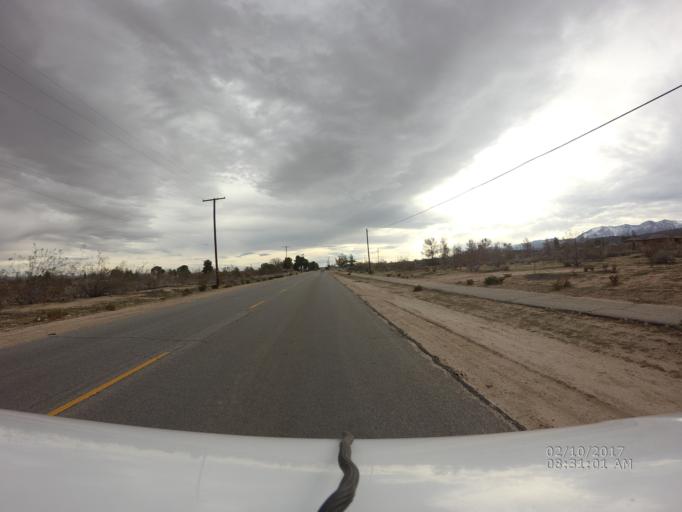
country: US
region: California
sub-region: Los Angeles County
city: Littlerock
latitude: 34.4992
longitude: -117.8985
